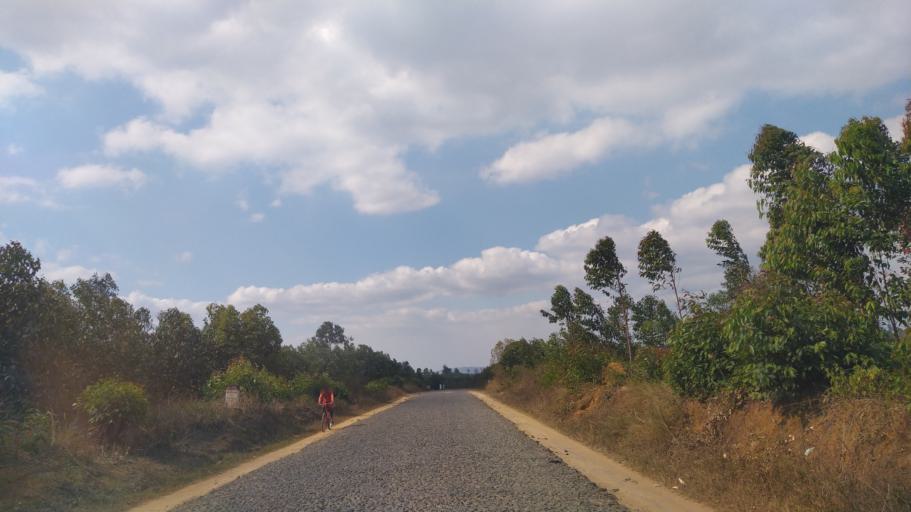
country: MG
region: Alaotra Mangoro
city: Moramanga
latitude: -18.7700
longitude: 48.2514
